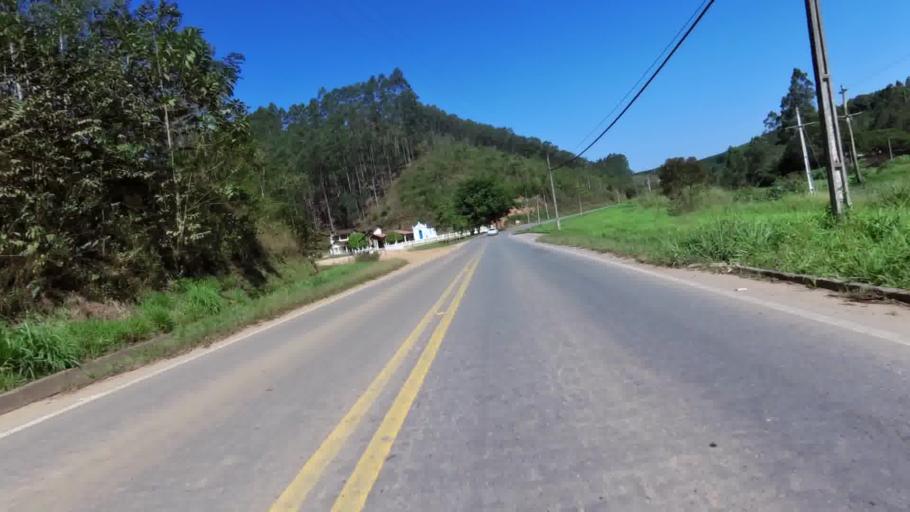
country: BR
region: Espirito Santo
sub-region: Marechal Floriano
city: Marechal Floriano
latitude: -20.4681
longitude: -40.7698
